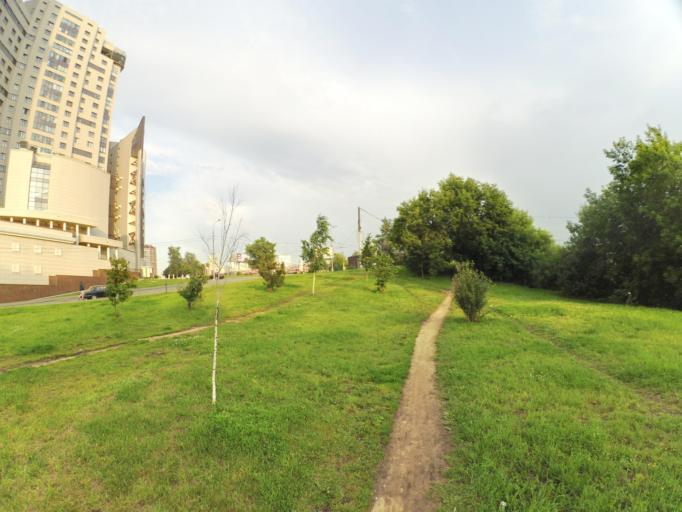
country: RU
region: Moscow
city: Shchukino
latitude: 55.7804
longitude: 37.4480
